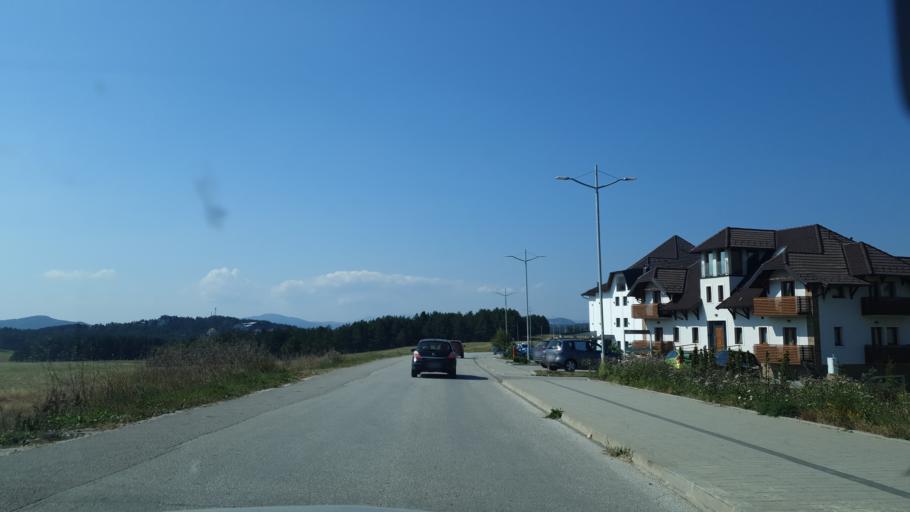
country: RS
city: Zlatibor
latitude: 43.7176
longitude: 19.7162
